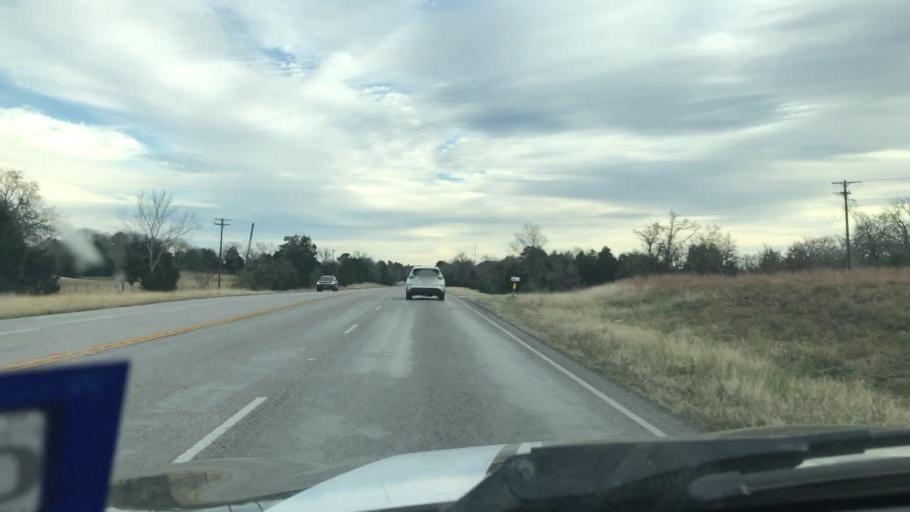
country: US
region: Texas
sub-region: Bastrop County
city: Camp Swift
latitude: 30.2714
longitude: -97.2365
